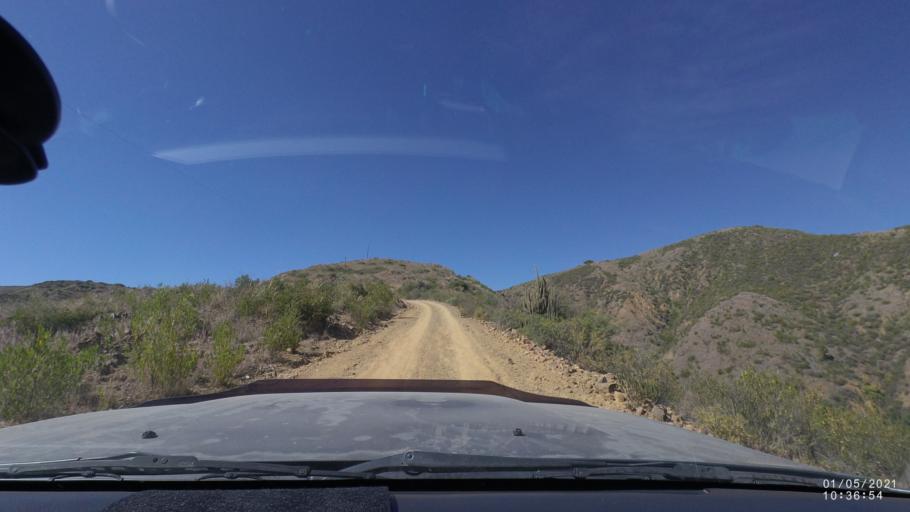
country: BO
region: Cochabamba
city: Capinota
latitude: -17.6005
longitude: -66.1875
